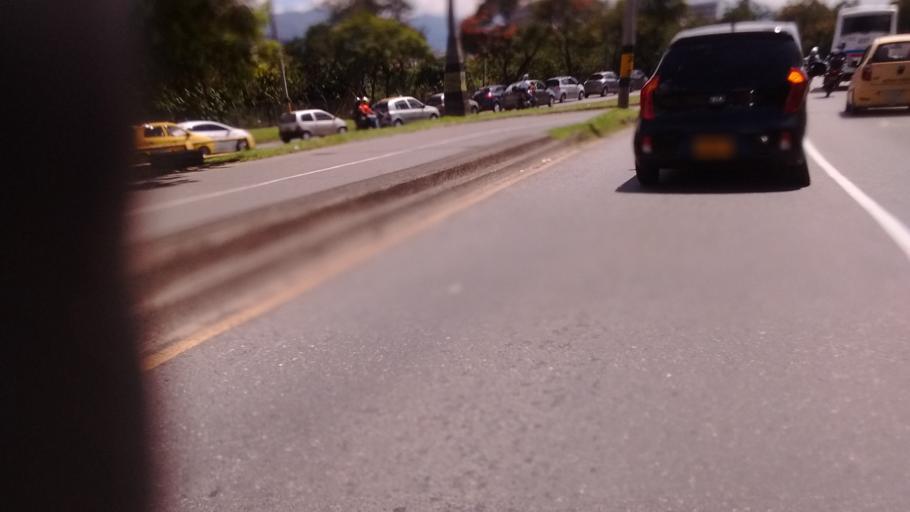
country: CO
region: Antioquia
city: Medellin
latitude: 6.2597
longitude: -75.5752
